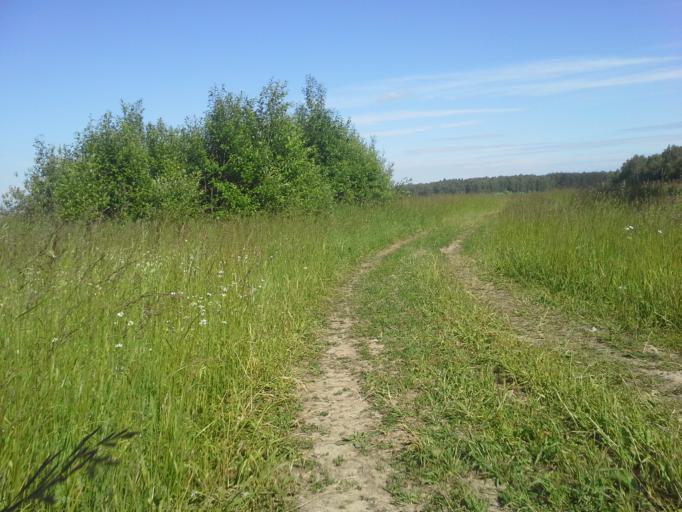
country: RU
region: Moskovskaya
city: Dubrovitsy
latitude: 55.4695
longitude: 37.4306
